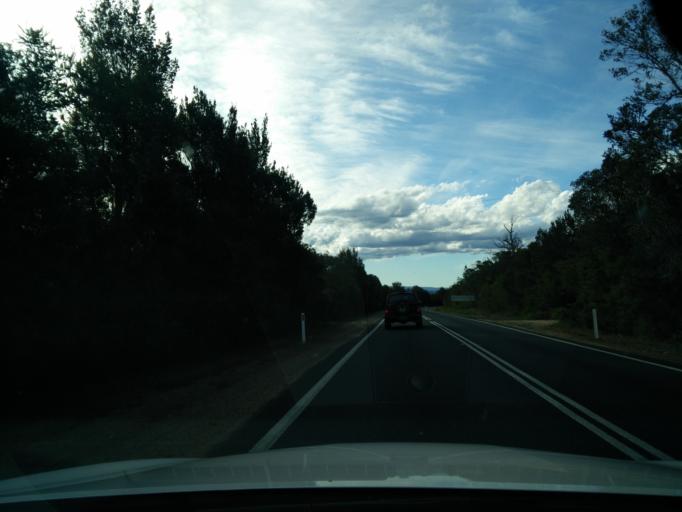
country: AU
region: Tasmania
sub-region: Break O'Day
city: St Helens
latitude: -42.0720
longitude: 148.2314
